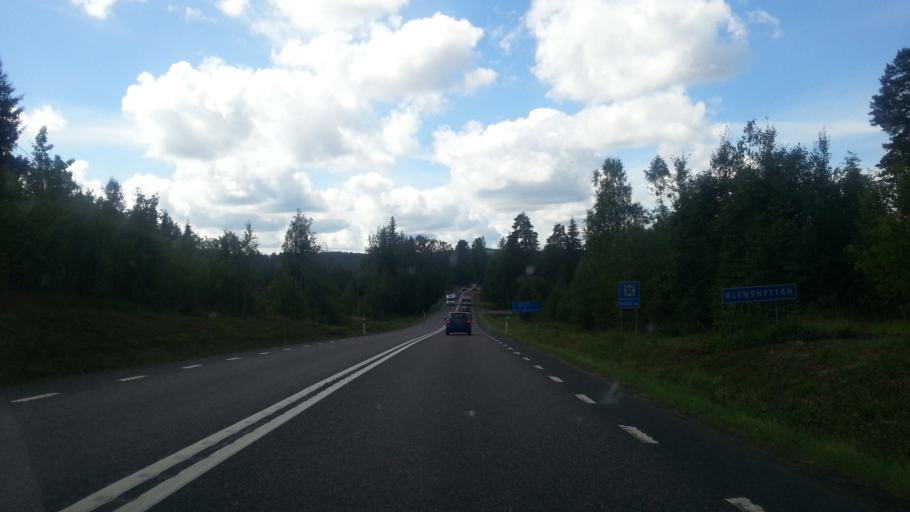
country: SE
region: Dalarna
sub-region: Ludvika Kommun
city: Ludvika
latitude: 60.1078
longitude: 15.1059
